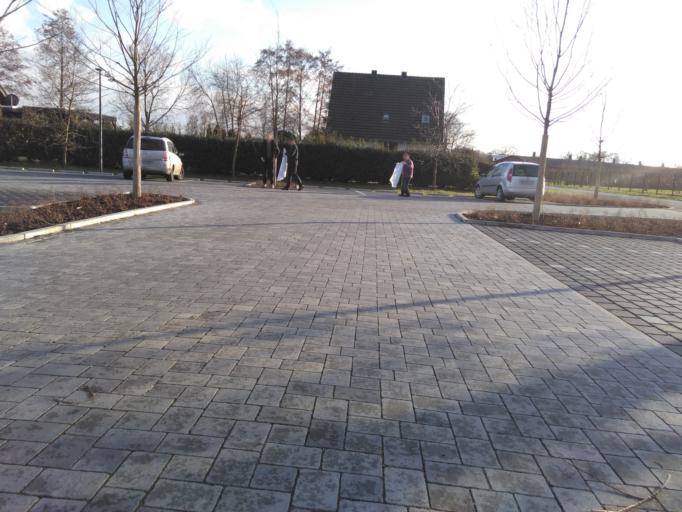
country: DE
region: North Rhine-Westphalia
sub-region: Regierungsbezirk Detmold
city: Verl
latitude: 51.8684
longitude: 8.4723
